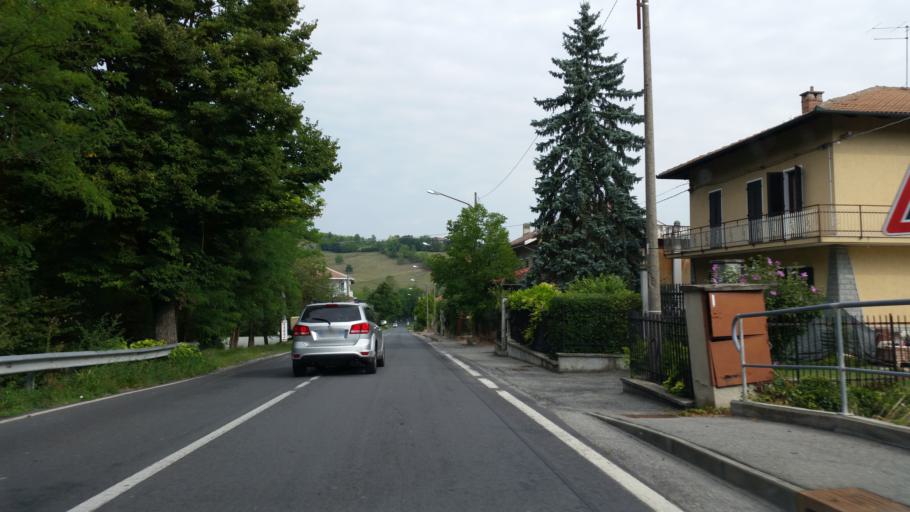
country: IT
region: Piedmont
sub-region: Provincia di Torino
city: Brozolo
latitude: 45.1209
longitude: 8.0599
